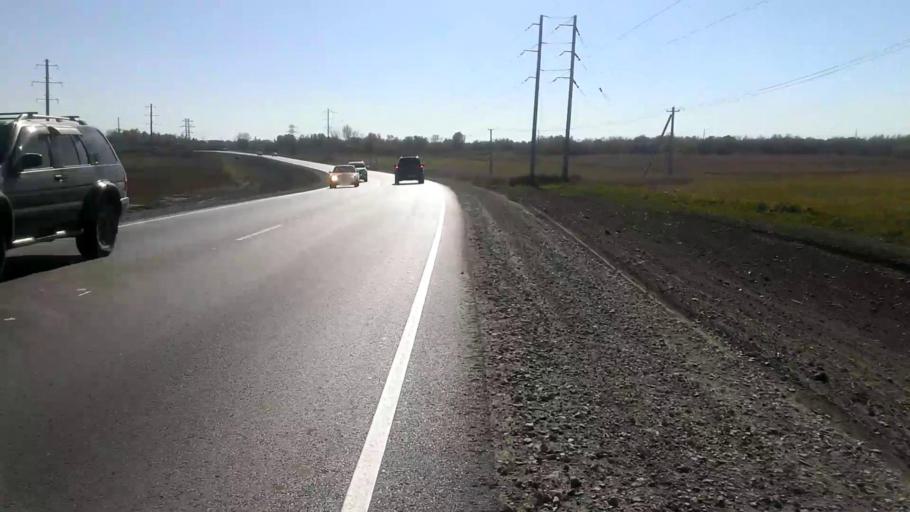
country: RU
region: Altai Krai
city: Sannikovo
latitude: 53.3336
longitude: 83.9379
